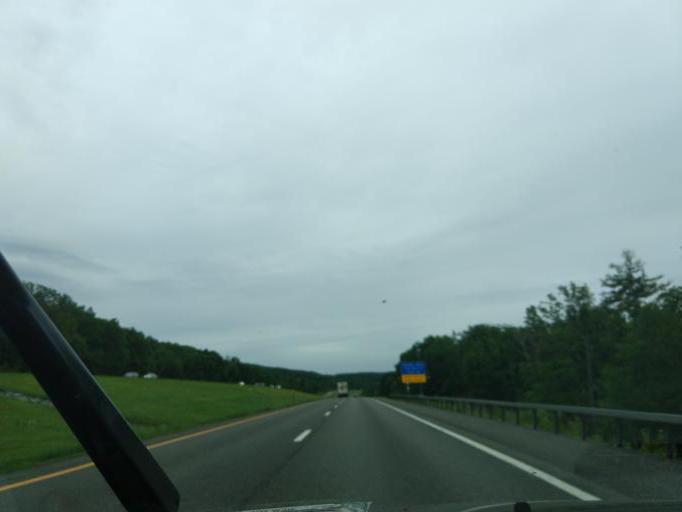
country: US
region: New York
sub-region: Broome County
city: Chenango Bridge
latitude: 42.2162
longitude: -75.9052
